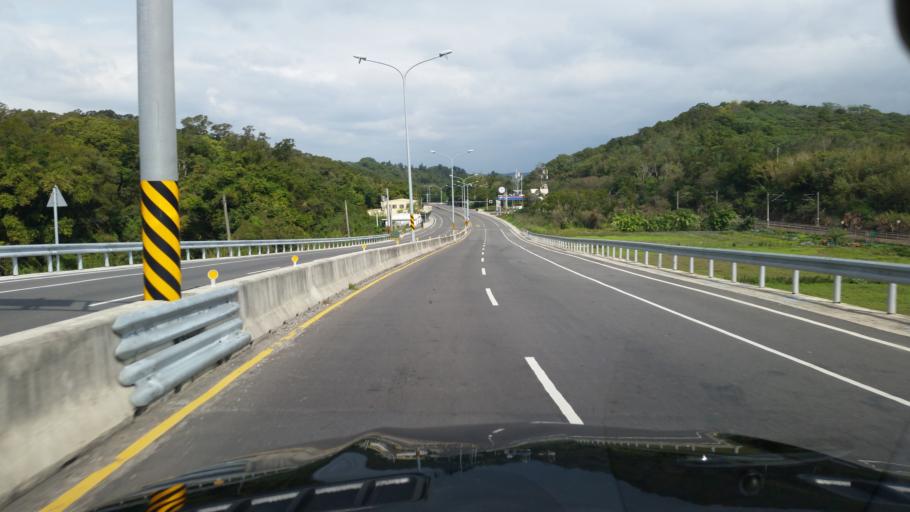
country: TW
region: Taiwan
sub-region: Miaoli
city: Miaoli
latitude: 24.6291
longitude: 120.8533
